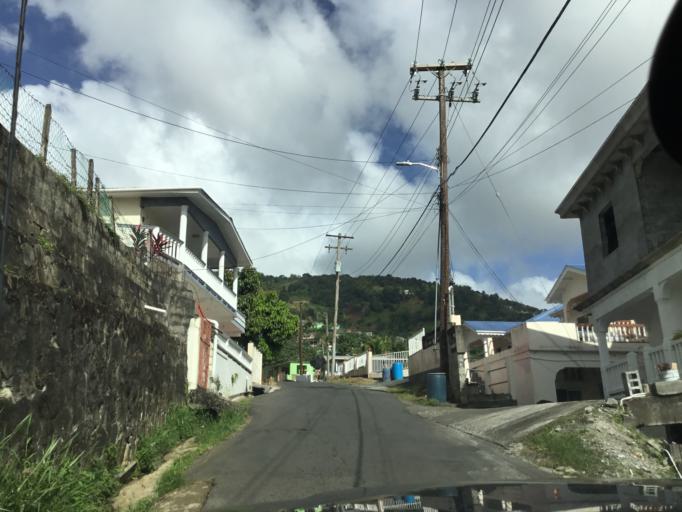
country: VC
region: Saint George
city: Kingstown
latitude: 13.1663
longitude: -61.2216
